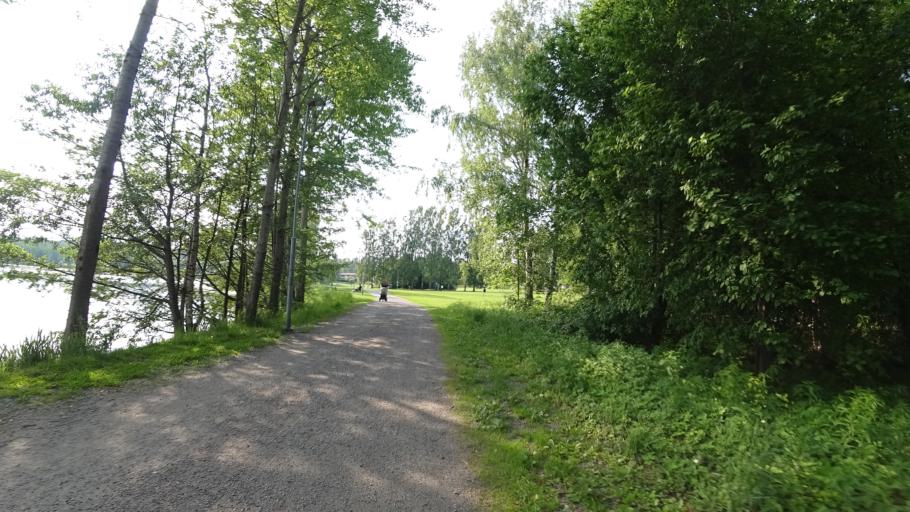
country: FI
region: Pirkanmaa
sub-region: Tampere
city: Pirkkala
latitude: 61.5054
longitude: 23.6733
